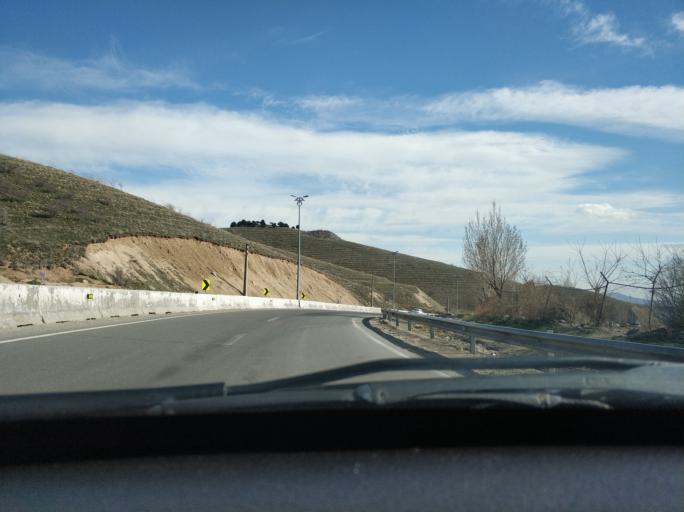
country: IR
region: Tehran
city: Tajrish
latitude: 35.8041
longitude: 51.5730
